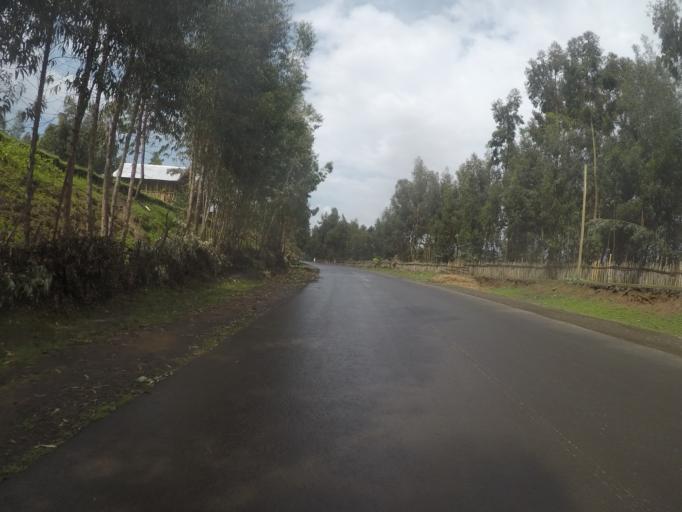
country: ET
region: Amhara
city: Debark'
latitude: 13.1191
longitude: 37.8811
